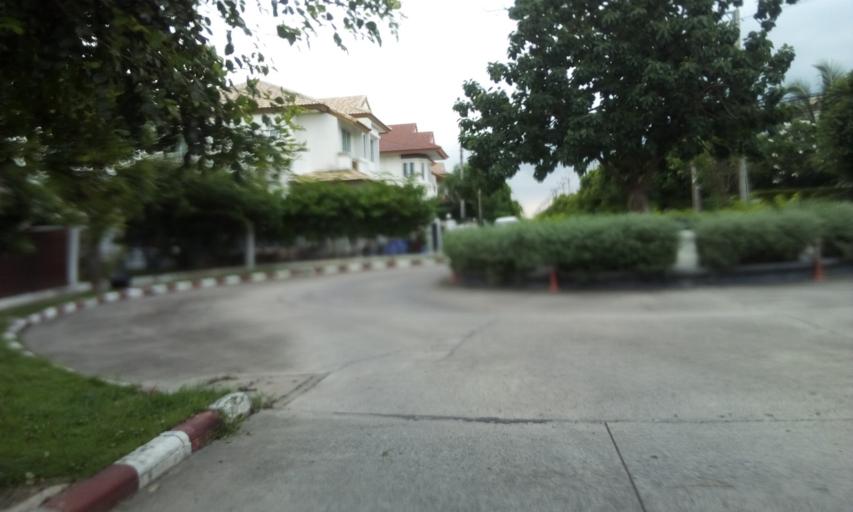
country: TH
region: Pathum Thani
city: Ban Rangsit
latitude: 14.0427
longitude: 100.8282
